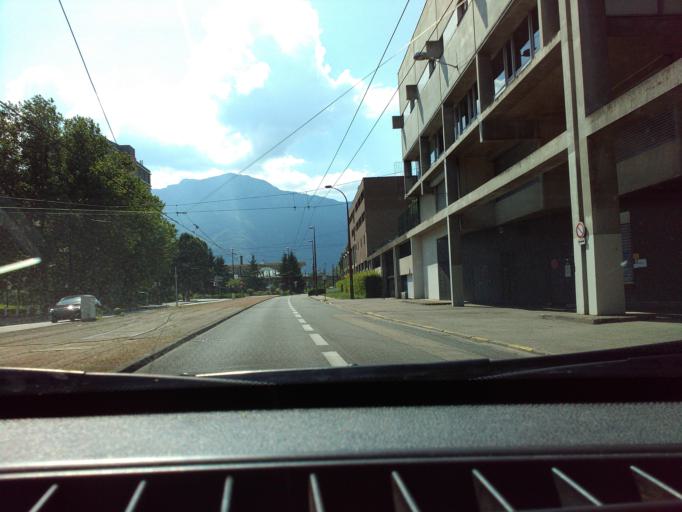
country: FR
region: Rhone-Alpes
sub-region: Departement de l'Isere
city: Echirolles
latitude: 45.1593
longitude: 5.7359
